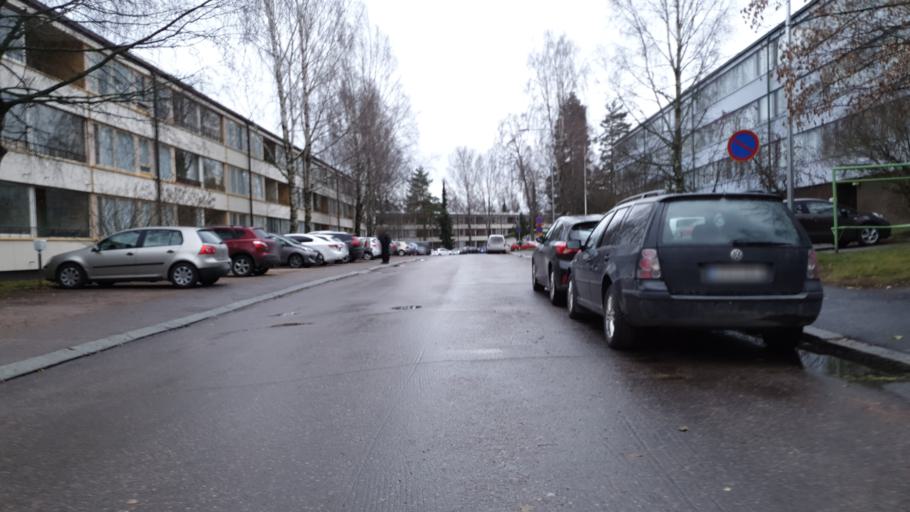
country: FI
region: Uusimaa
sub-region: Helsinki
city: Teekkarikylae
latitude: 60.2711
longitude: 24.8707
